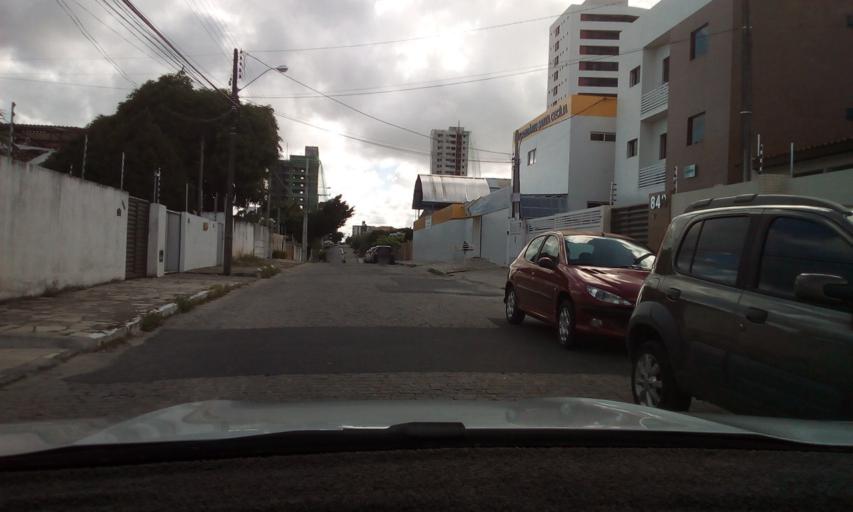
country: BR
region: Paraiba
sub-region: Joao Pessoa
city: Joao Pessoa
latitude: -7.1235
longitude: -34.8398
